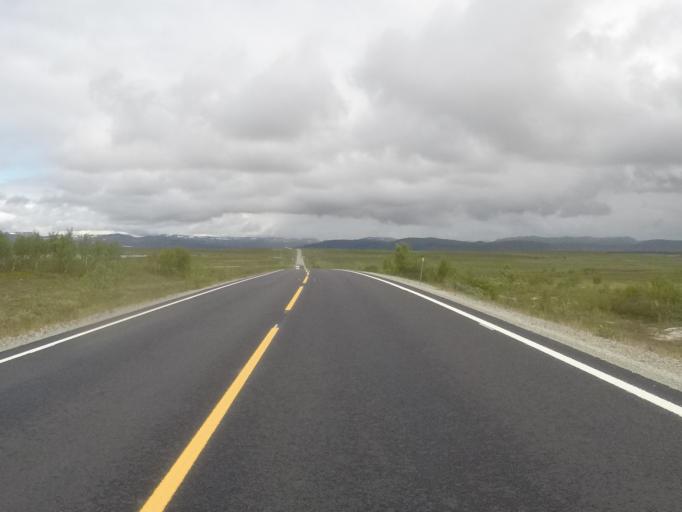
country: NO
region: Finnmark Fylke
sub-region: Kvalsund
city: Kvalsund
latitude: 70.2081
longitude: 24.0699
